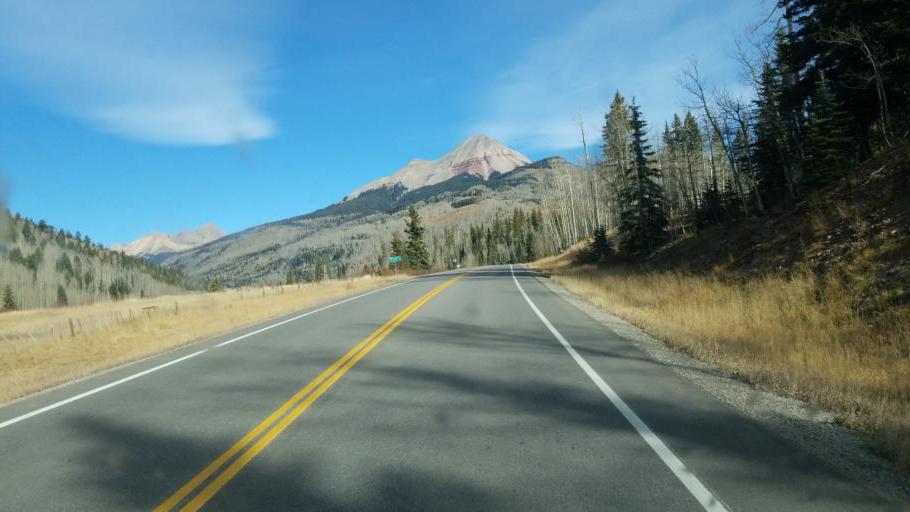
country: US
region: Colorado
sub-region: San Juan County
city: Silverton
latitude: 37.6443
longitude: -107.8071
